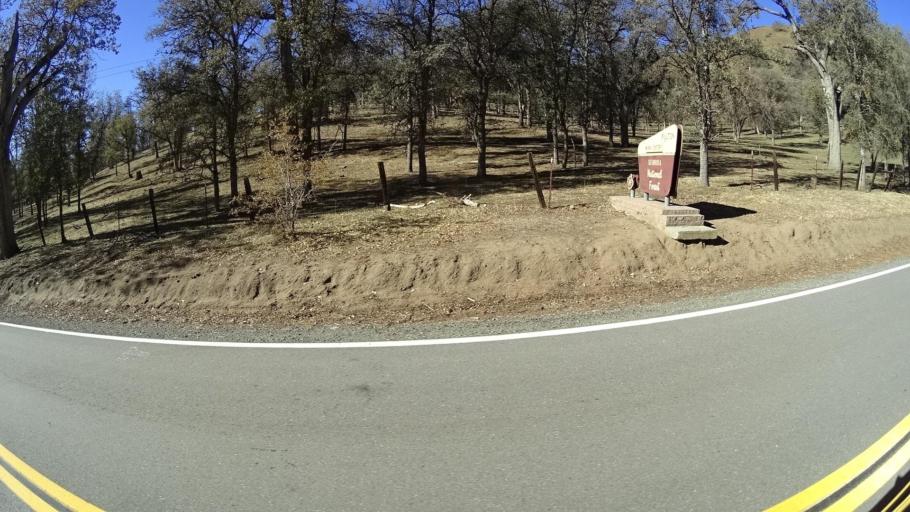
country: US
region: California
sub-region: Kern County
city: Alta Sierra
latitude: 35.7242
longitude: -118.6803
